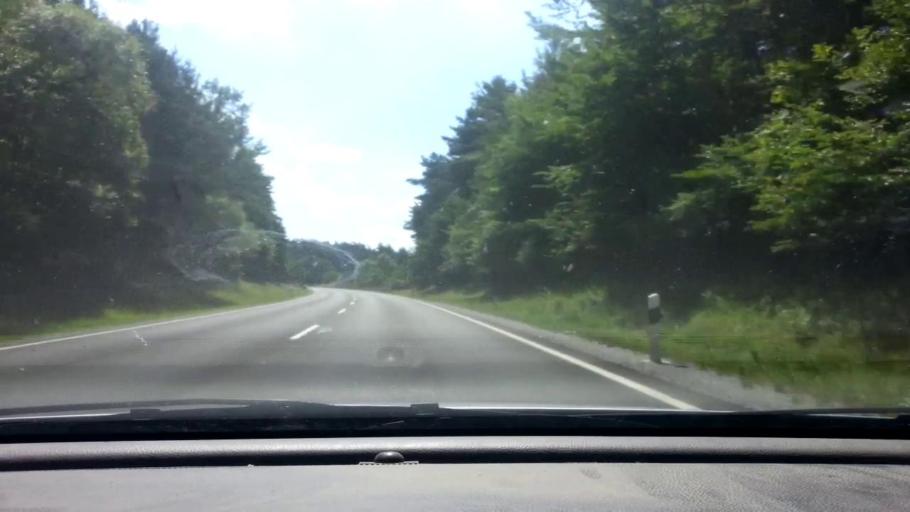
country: DE
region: Bavaria
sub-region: Upper Franconia
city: Seybothenreuth
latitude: 49.8896
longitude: 11.7168
